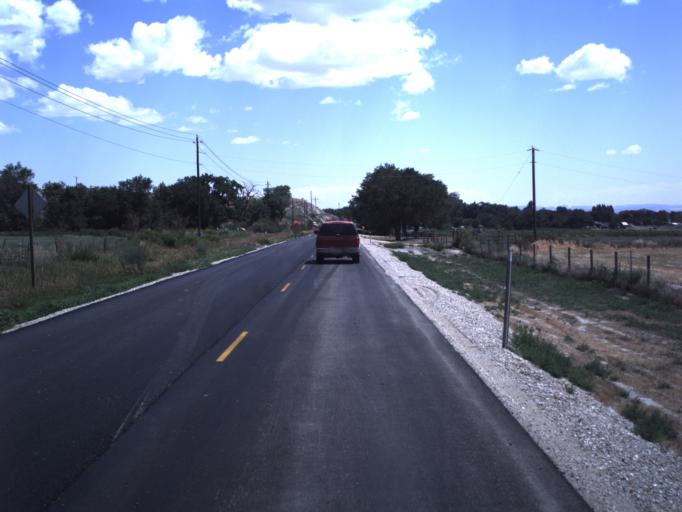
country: US
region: Utah
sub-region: Emery County
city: Orangeville
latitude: 39.2405
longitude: -111.0599
